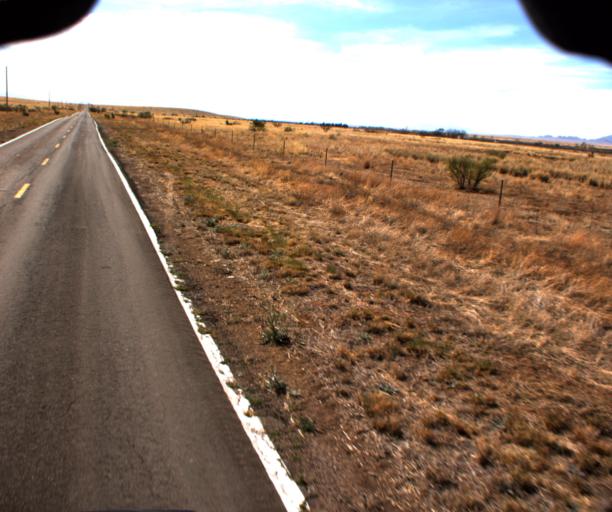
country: US
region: Arizona
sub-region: Cochise County
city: Willcox
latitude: 32.0067
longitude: -109.4093
